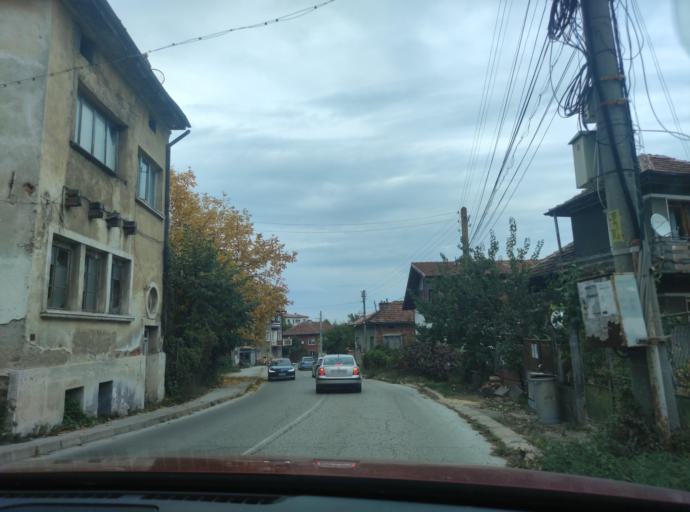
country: BG
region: Montana
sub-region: Obshtina Berkovitsa
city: Berkovitsa
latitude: 43.1987
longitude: 23.1614
